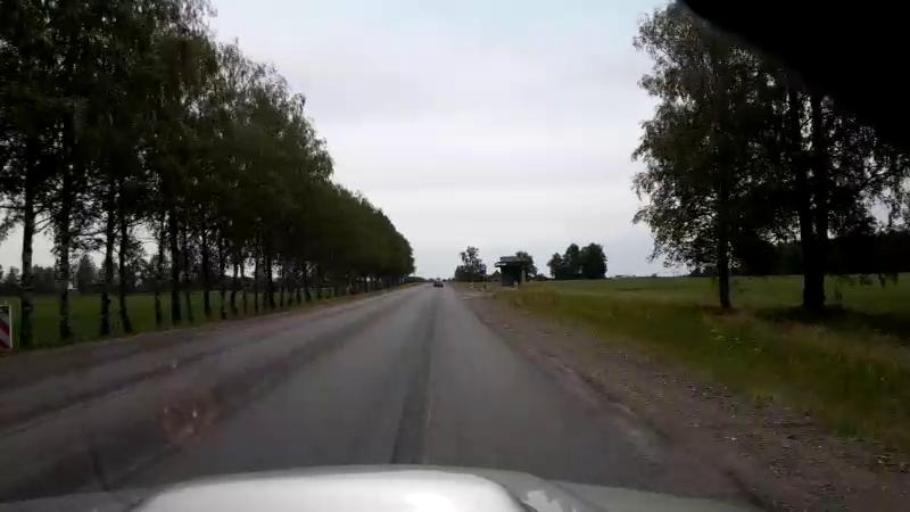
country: LV
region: Bauskas Rajons
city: Bauska
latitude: 56.3773
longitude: 24.2647
